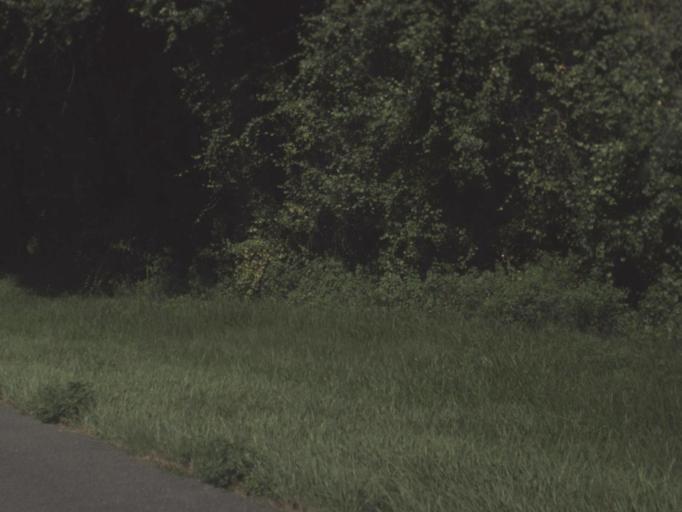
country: US
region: Florida
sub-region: Pasco County
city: Saint Leo
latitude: 28.3390
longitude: -82.2340
